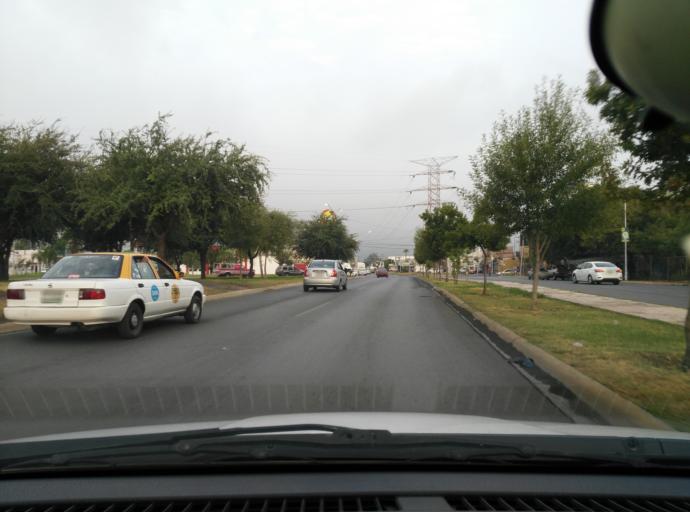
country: MX
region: Nuevo Leon
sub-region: San Nicolas de los Garza
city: San Nicolas de los Garza
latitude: 25.7711
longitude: -100.2625
